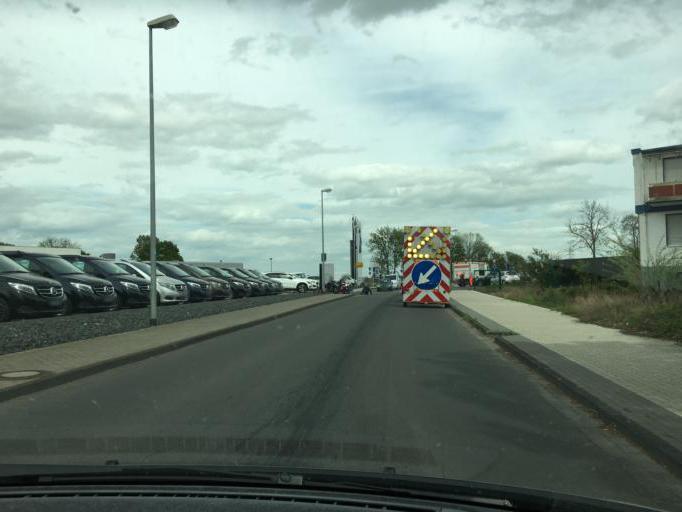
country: DE
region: North Rhine-Westphalia
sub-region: Regierungsbezirk Koln
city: Euskirchen
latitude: 50.6683
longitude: 6.8062
